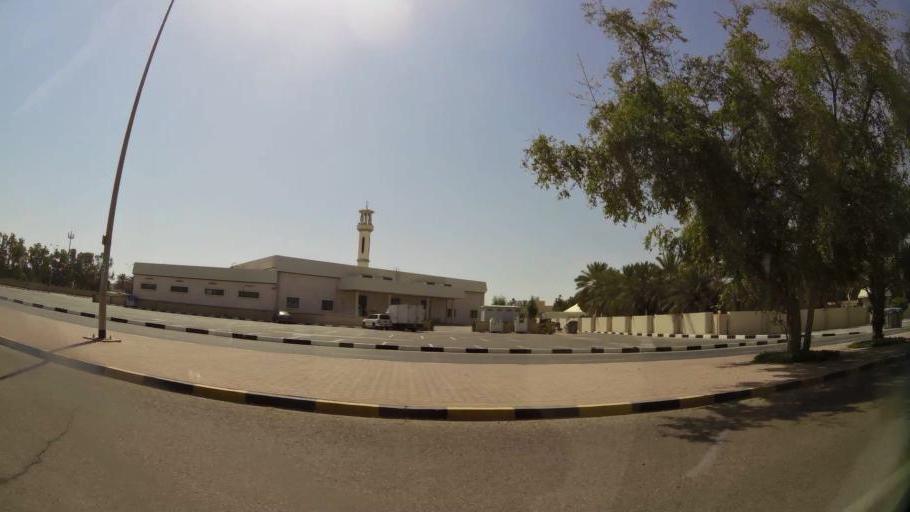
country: AE
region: Ajman
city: Ajman
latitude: 25.4092
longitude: 55.4739
